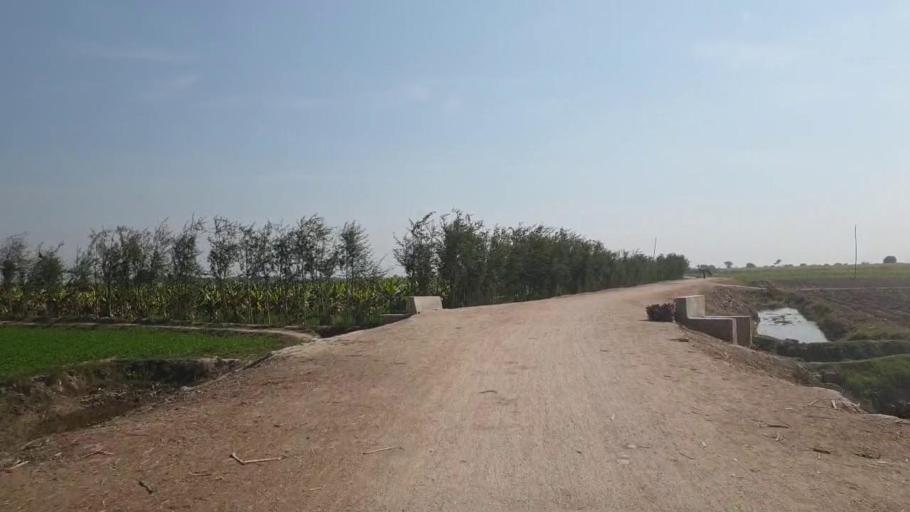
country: PK
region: Sindh
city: Chambar
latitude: 25.3495
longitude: 68.8299
